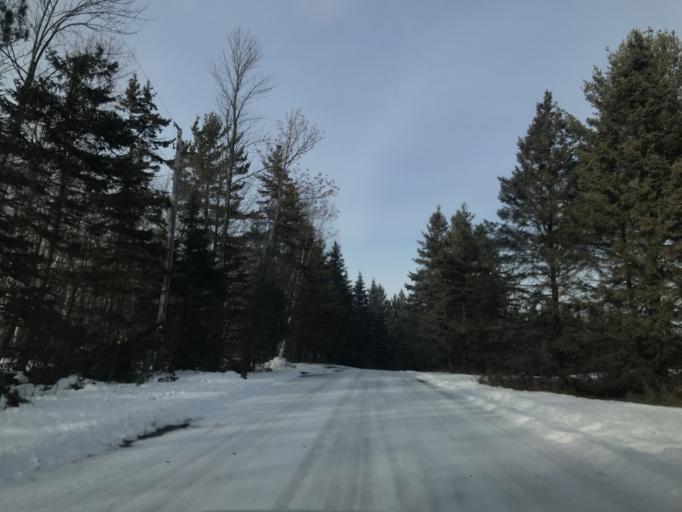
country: US
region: Wisconsin
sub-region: Door County
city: Sturgeon Bay
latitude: 45.1484
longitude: -87.0541
